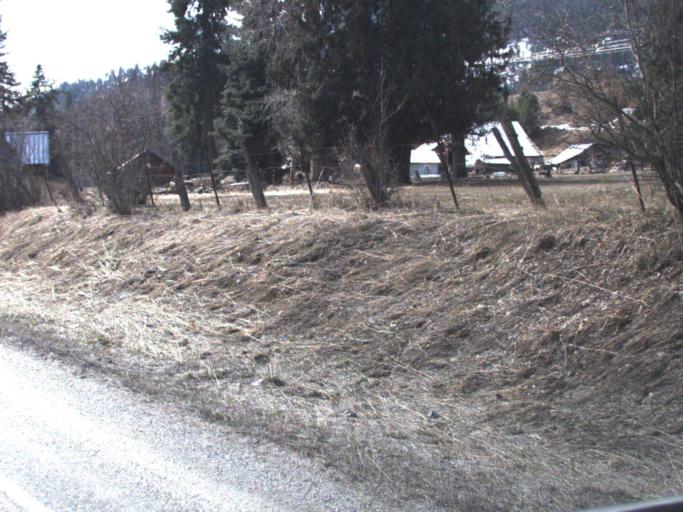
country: US
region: Washington
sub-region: Stevens County
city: Chewelah
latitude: 48.6102
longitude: -117.3645
